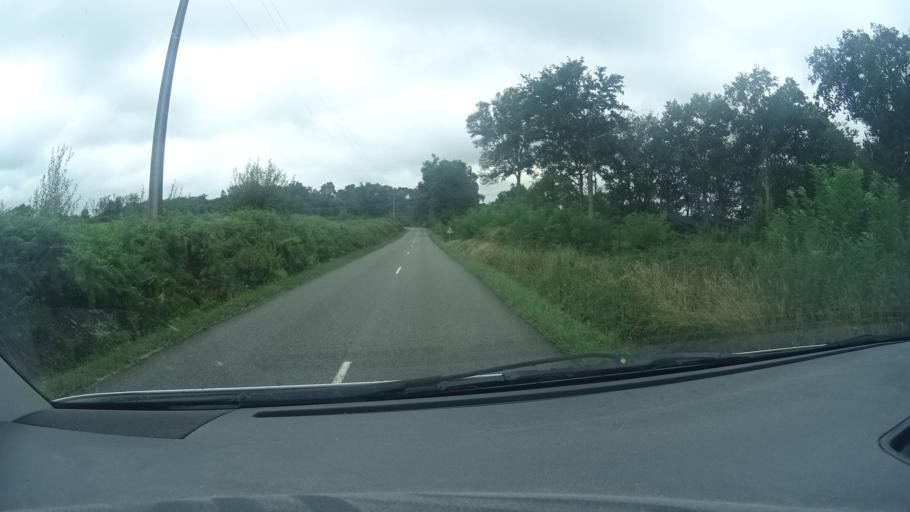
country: FR
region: Aquitaine
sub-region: Departement des Pyrenees-Atlantiques
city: Mont
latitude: 43.4890
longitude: -0.6816
